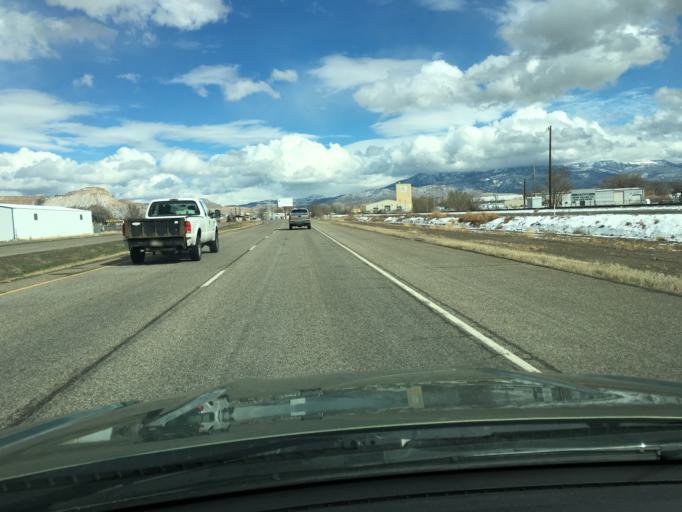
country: US
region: Colorado
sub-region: Mesa County
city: Fruitvale
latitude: 39.0754
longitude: -108.5039
